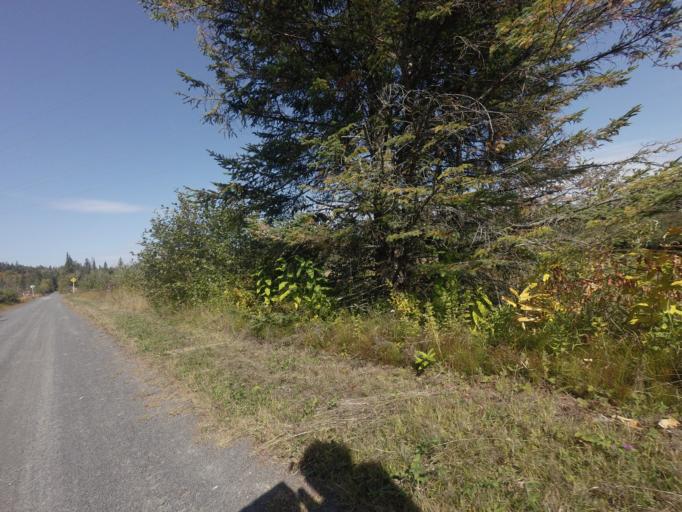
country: CA
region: Quebec
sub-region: Laurentides
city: Sainte-Agathe-des-Monts
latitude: 46.0881
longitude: -74.3422
